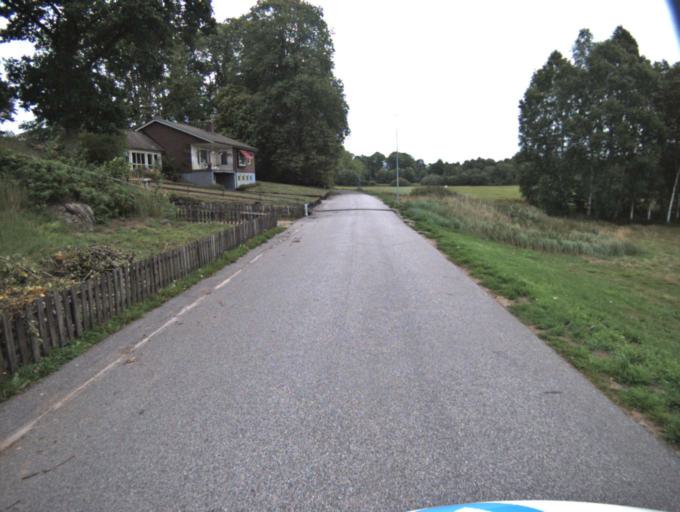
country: SE
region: Vaestra Goetaland
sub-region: Ulricehamns Kommun
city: Ulricehamn
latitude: 57.8427
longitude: 13.2842
